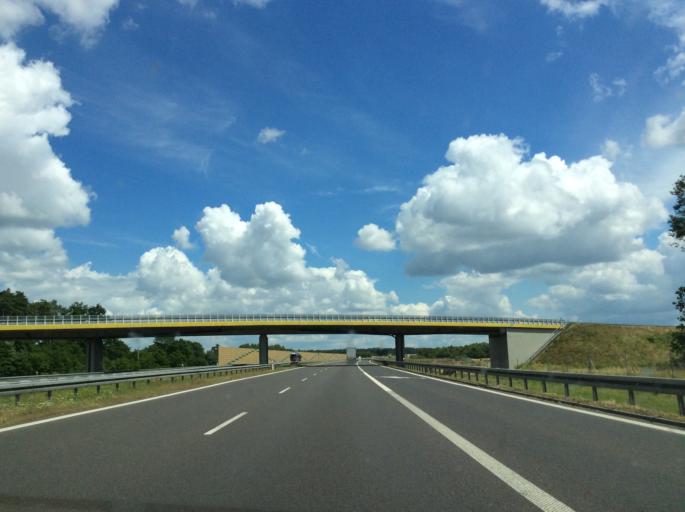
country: PL
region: Greater Poland Voivodeship
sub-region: Powiat koninski
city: Krzymow
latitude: 52.1524
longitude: 18.4587
